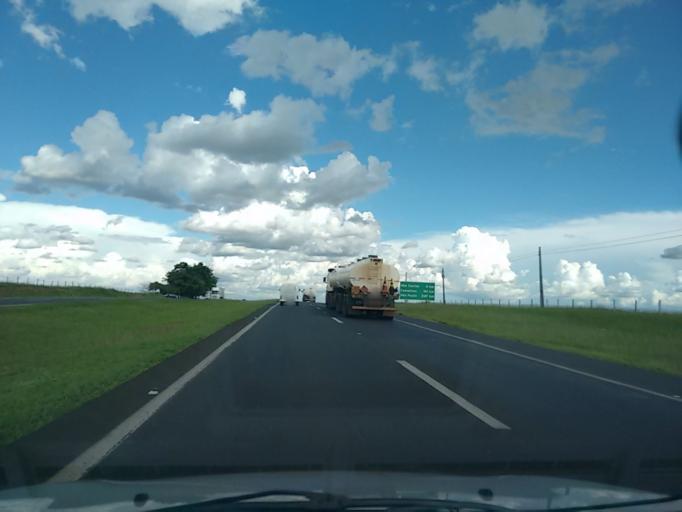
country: BR
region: Sao Paulo
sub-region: Ibate
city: Ibate
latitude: -21.9580
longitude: -47.9826
